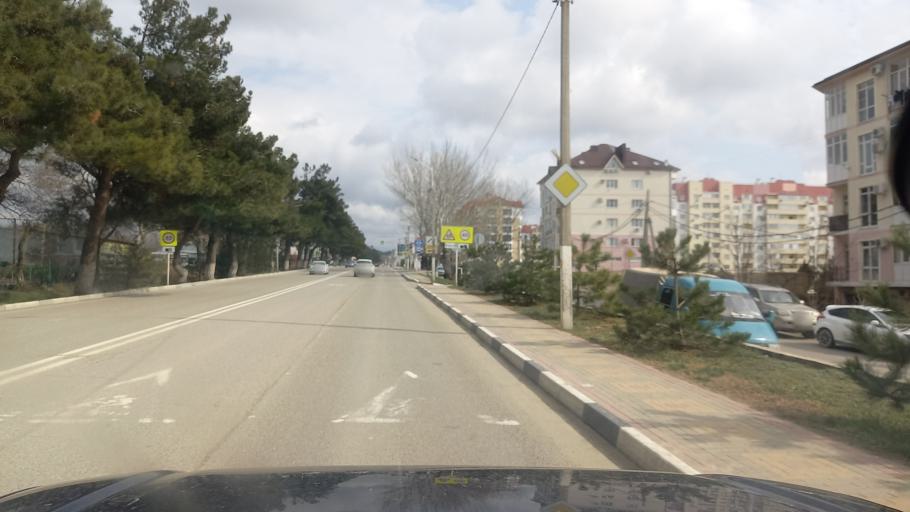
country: RU
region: Krasnodarskiy
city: Gelendzhik
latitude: 44.5584
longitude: 38.0999
